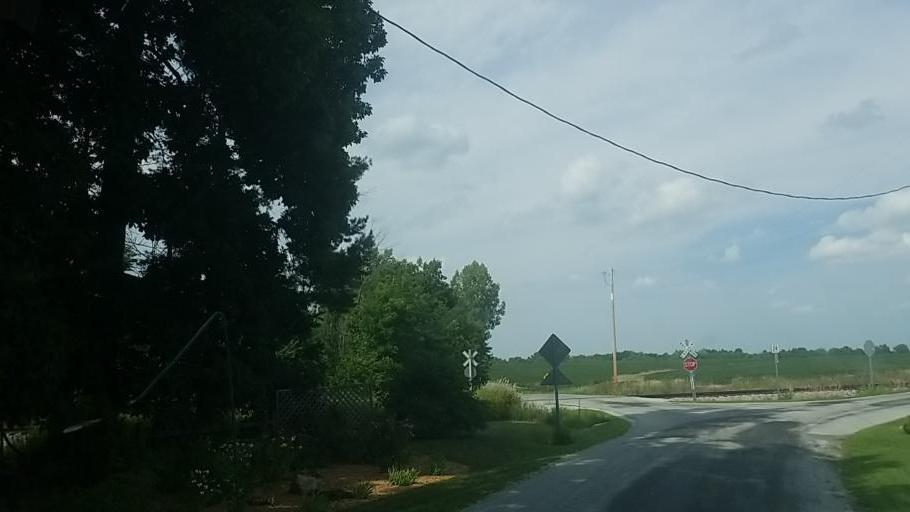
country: US
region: Ohio
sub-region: Hardin County
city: Forest
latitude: 40.7980
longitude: -83.5510
